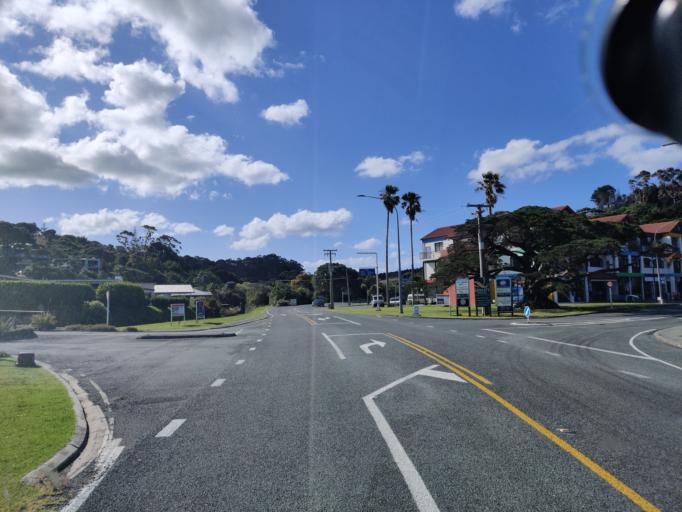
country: NZ
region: Northland
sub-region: Whangarei
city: Ngunguru
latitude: -35.6108
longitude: 174.5245
